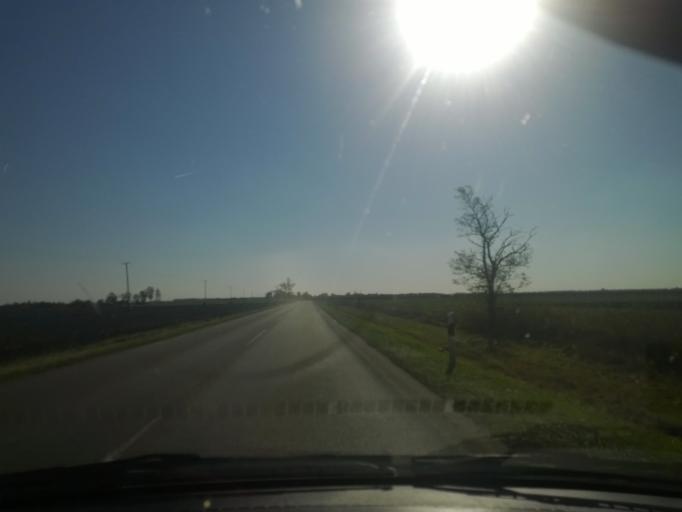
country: HU
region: Csongrad
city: Szegvar
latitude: 46.5710
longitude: 20.3083
